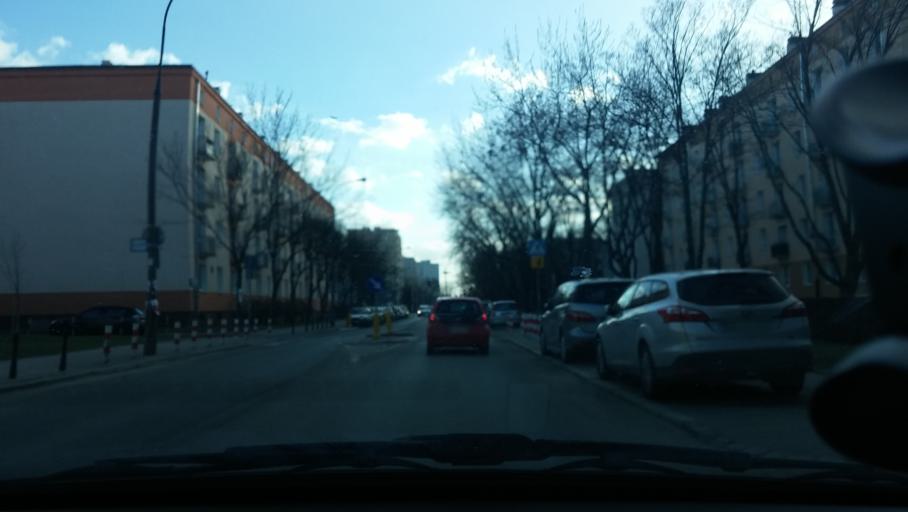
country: PL
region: Masovian Voivodeship
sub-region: Warszawa
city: Ochota
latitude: 52.2086
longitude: 20.9692
